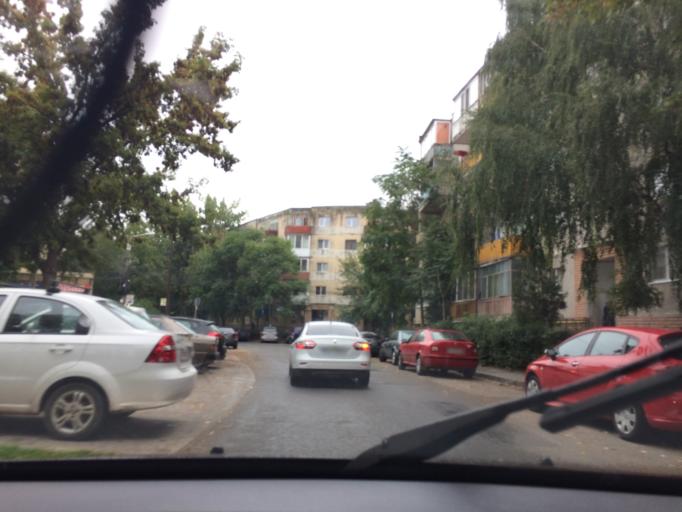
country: RO
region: Timis
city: Timisoara
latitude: 45.7520
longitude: 21.2417
